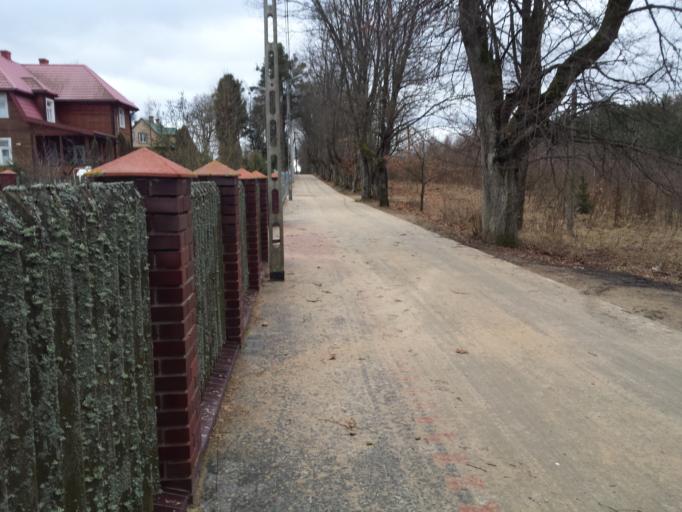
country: PL
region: Podlasie
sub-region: Powiat hajnowski
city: Bialowieza
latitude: 52.7000
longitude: 23.8827
